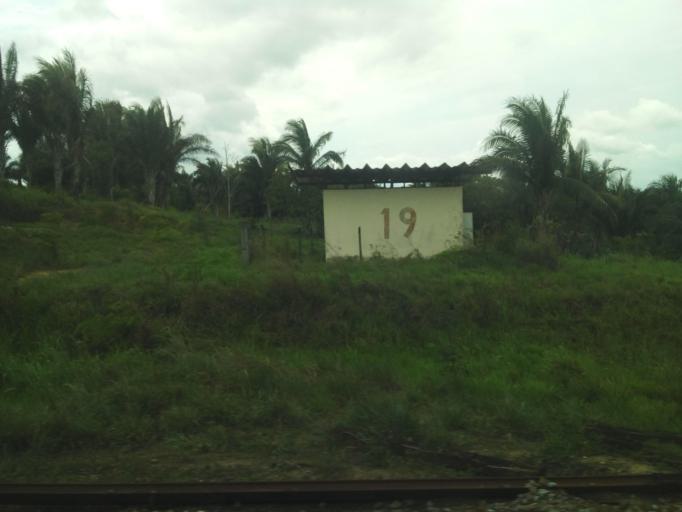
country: BR
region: Maranhao
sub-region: Santa Ines
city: Santa Ines
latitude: -3.7457
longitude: -46.1186
